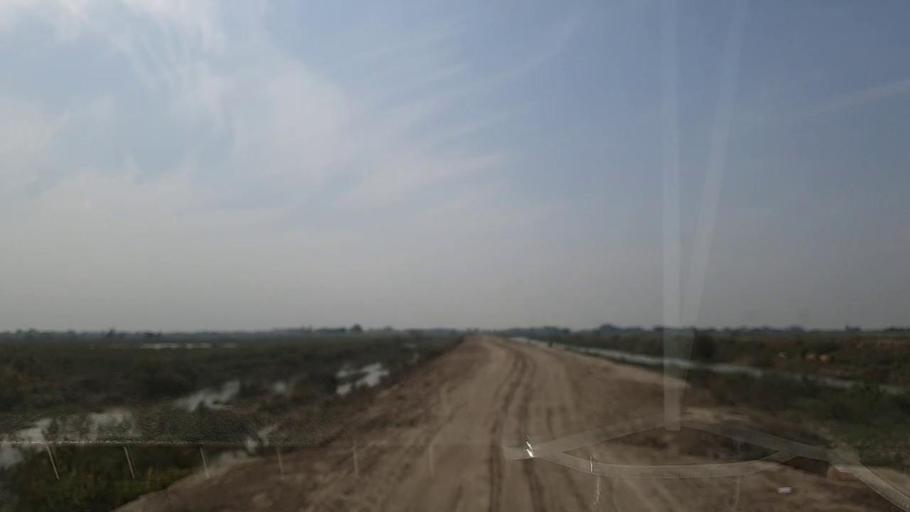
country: PK
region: Sindh
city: Mirpur Batoro
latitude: 24.6474
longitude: 68.2294
